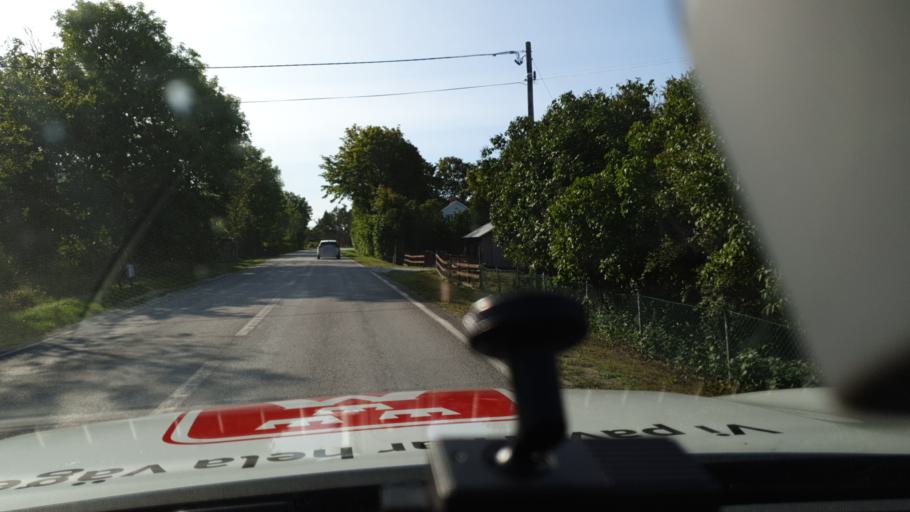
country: SE
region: Gotland
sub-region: Gotland
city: Klintehamn
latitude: 57.3285
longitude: 18.1931
